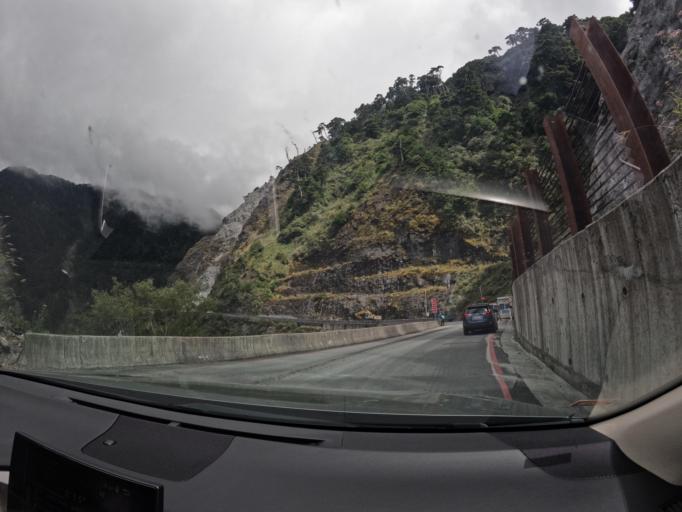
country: TW
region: Taiwan
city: Yujing
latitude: 23.2658
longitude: 120.9503
